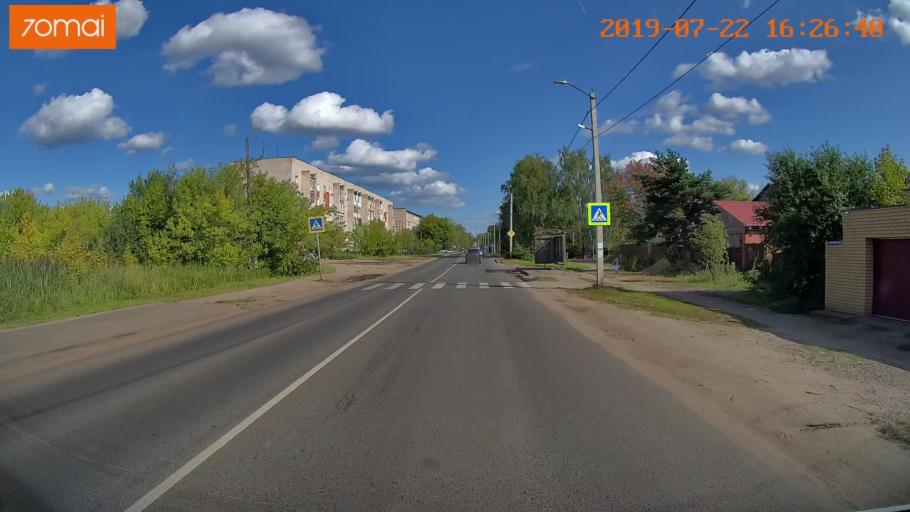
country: RU
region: Ivanovo
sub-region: Gorod Ivanovo
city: Ivanovo
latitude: 57.0479
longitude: 40.9372
